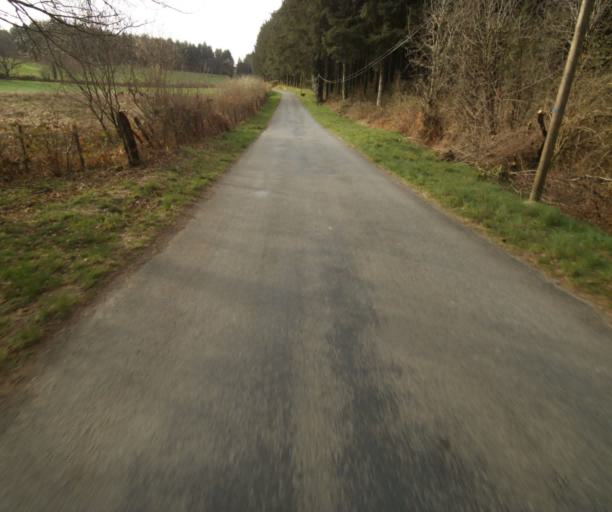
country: FR
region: Limousin
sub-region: Departement de la Correze
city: Treignac
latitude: 45.4648
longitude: 1.8122
